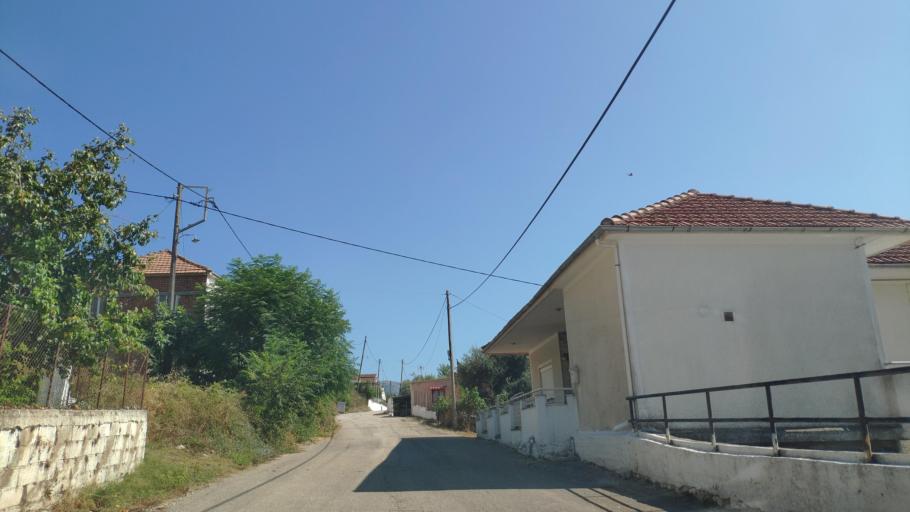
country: GR
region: Epirus
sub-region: Nomos Prevezis
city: Kanalaki
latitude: 39.2756
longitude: 20.5988
